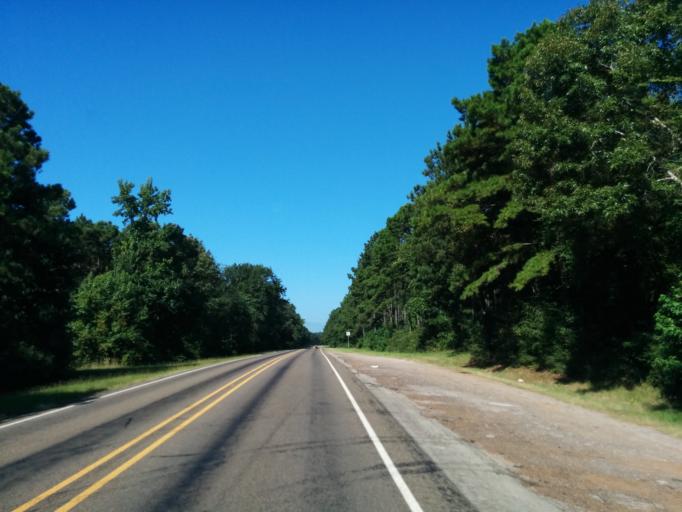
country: US
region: Texas
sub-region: Sabine County
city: Milam
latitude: 31.4330
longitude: -93.7906
